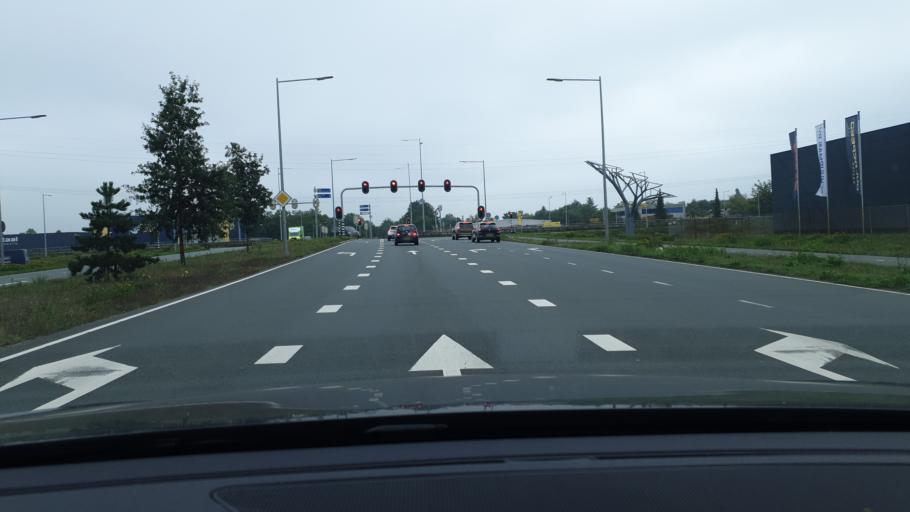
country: NL
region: North Brabant
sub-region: Gemeente Oss
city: Berghem
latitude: 51.7556
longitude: 5.5548
